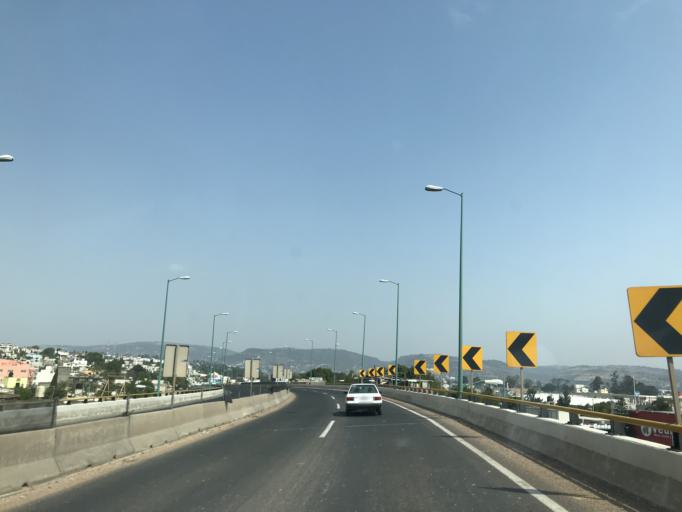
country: MX
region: Tlaxcala
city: Tlaxcala de Xicohtencatl
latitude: 19.3112
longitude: -98.2008
